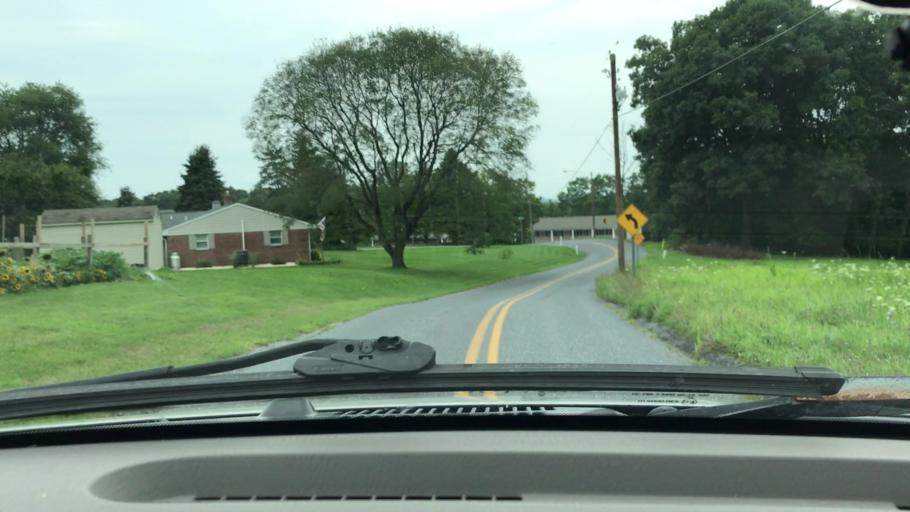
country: US
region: Pennsylvania
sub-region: Lancaster County
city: Elizabethtown
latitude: 40.1716
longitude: -76.6091
